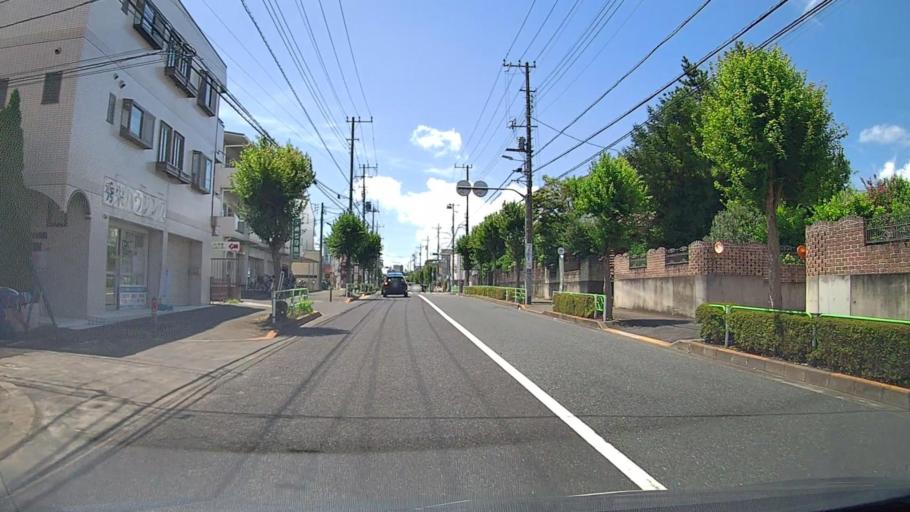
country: JP
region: Tokyo
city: Nishi-Tokyo-shi
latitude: 35.7392
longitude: 139.5659
